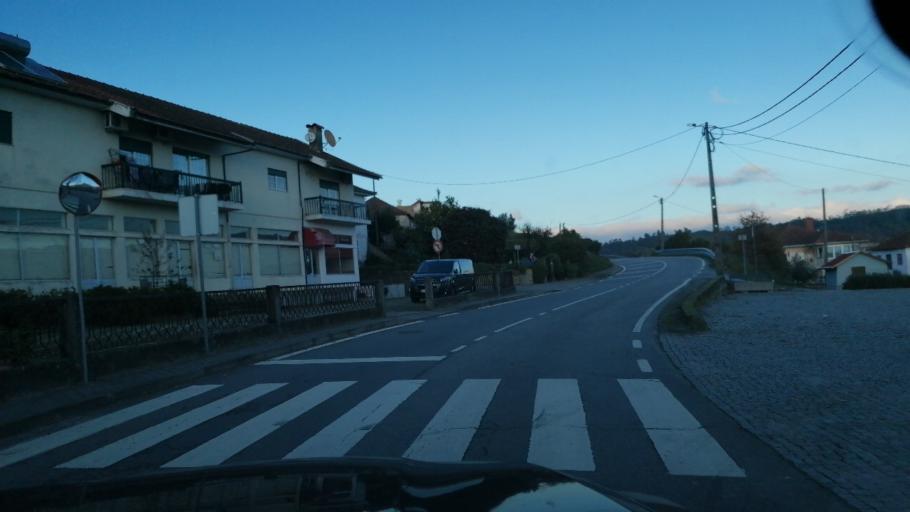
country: PT
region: Vila Real
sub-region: Mondim de Basto
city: Mondim de Basto
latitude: 41.4433
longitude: -7.9661
